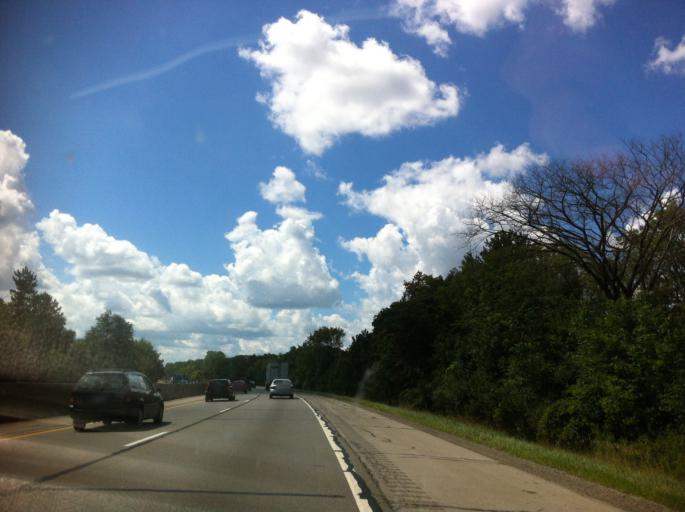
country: US
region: Michigan
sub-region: Washtenaw County
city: Ann Arbor
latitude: 42.2358
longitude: -83.7072
